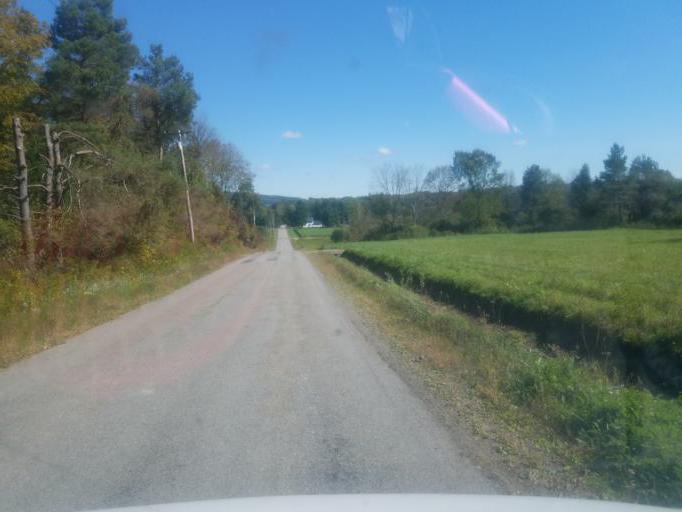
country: US
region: New York
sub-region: Allegany County
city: Friendship
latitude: 42.3149
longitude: -78.1155
